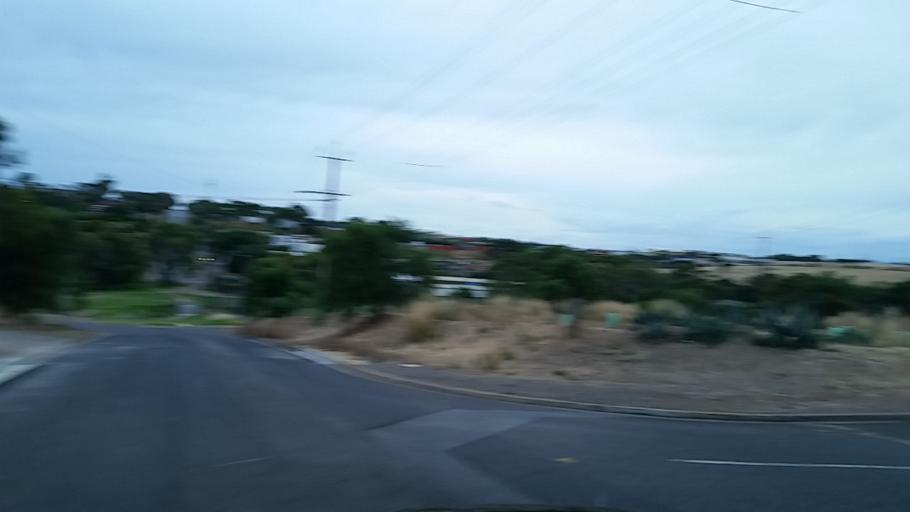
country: AU
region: South Australia
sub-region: Adelaide
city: Port Noarlunga
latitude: -35.1256
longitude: 138.4852
